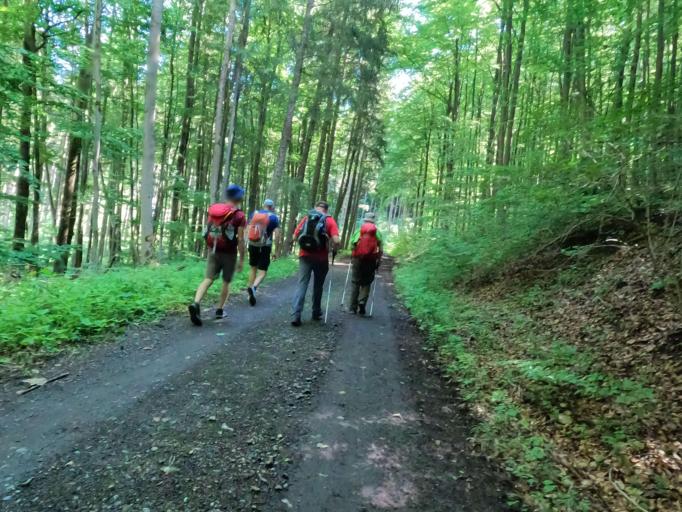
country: DE
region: Bavaria
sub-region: Regierungsbezirk Unterfranken
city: Zeitlofs
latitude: 50.3286
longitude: 9.6360
